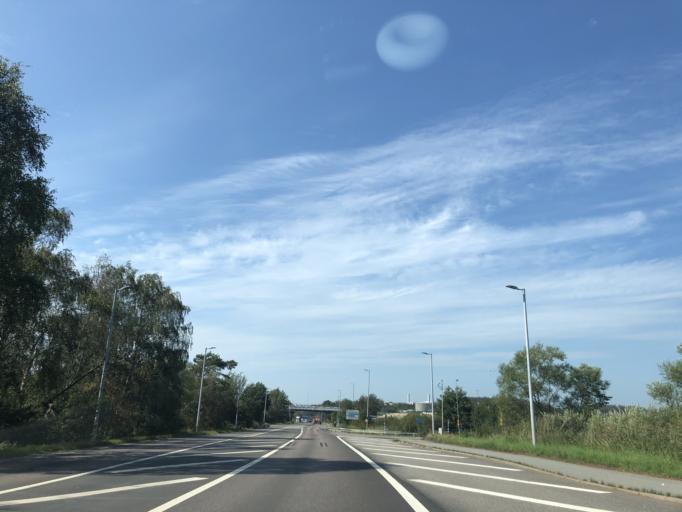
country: SE
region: Vaestra Goetaland
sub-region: Goteborg
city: Majorna
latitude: 57.6999
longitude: 11.8655
